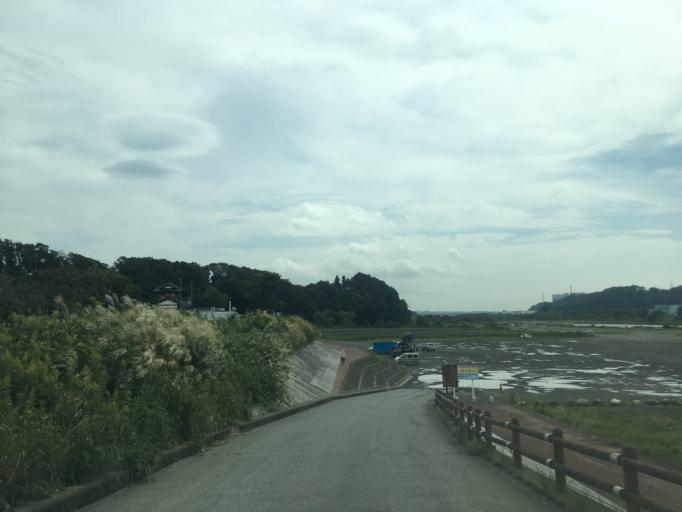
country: JP
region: Kanagawa
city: Zama
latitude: 35.5421
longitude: 139.3322
